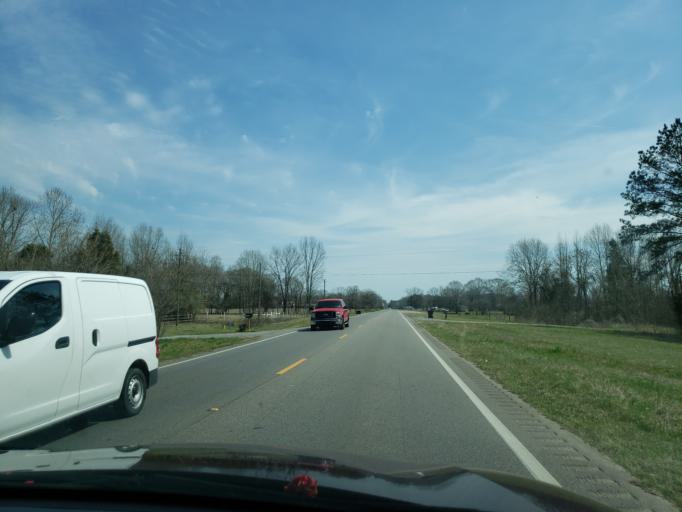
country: US
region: Alabama
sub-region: Autauga County
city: Prattville
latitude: 32.4307
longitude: -86.5159
